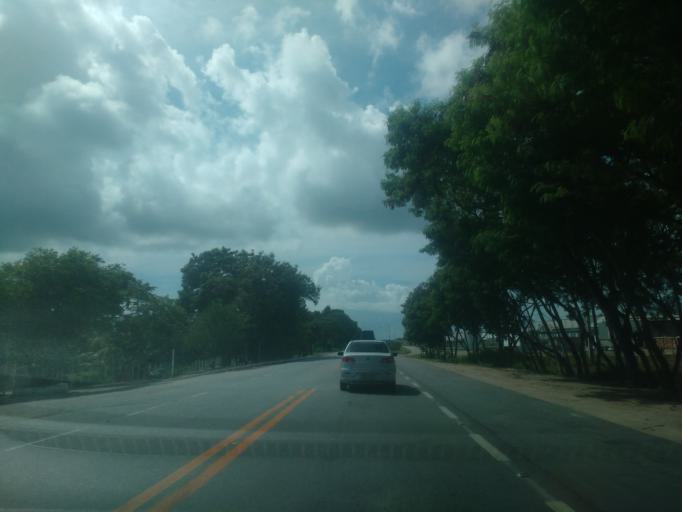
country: BR
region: Alagoas
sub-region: Marechal Deodoro
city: Marechal Deodoro
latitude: -9.6814
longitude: -35.8303
